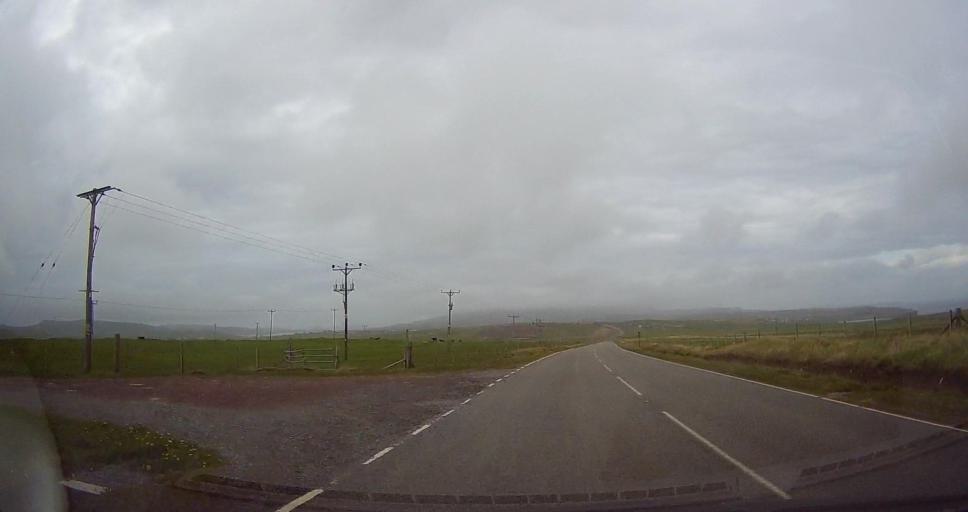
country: GB
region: Scotland
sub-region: Shetland Islands
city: Sandwick
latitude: 59.8977
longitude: -1.3036
